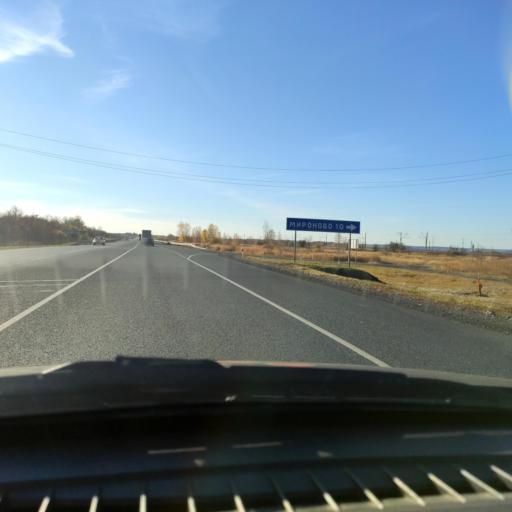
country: RU
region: Samara
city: Obsharovka
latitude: 53.2384
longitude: 48.9586
